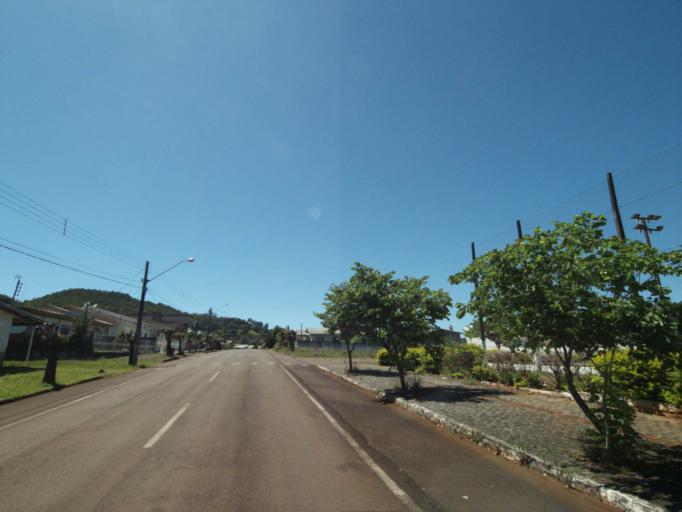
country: BR
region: Parana
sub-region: Pato Branco
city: Pato Branco
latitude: -26.2656
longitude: -52.7779
